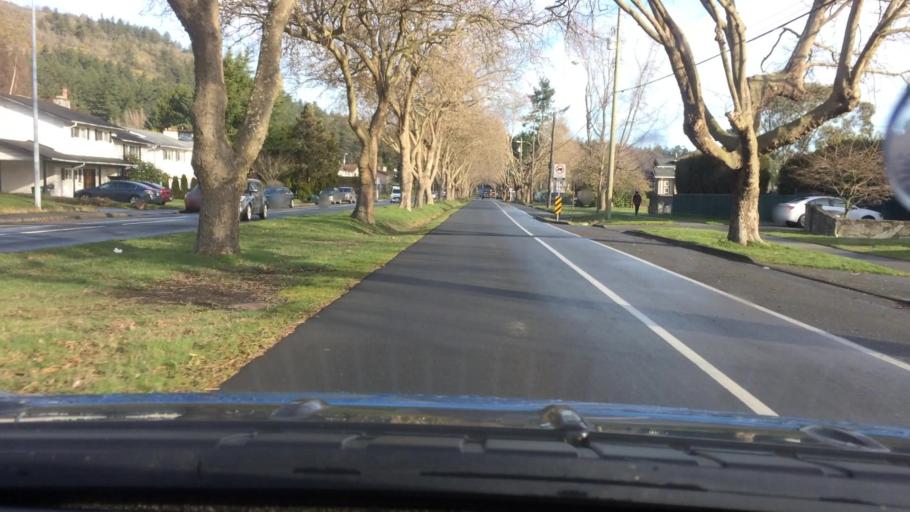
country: CA
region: British Columbia
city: Oak Bay
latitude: 48.4849
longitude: -123.3370
